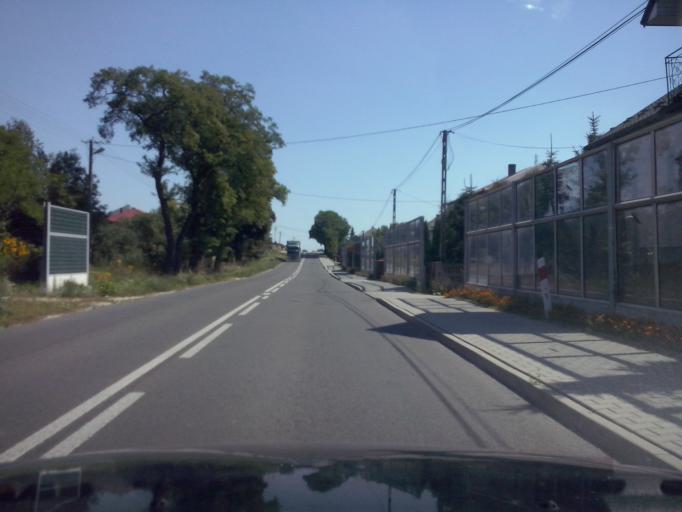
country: PL
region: Swietokrzyskie
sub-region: Powiat kielecki
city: Chmielnik
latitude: 50.6088
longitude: 20.7970
